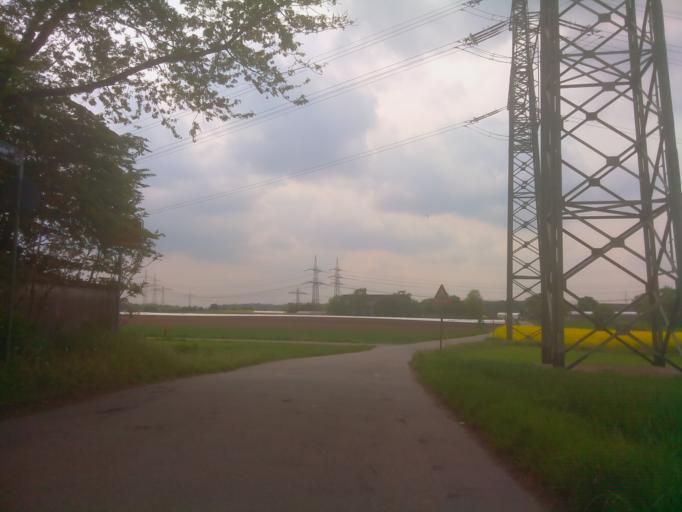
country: DE
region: Baden-Wuerttemberg
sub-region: Karlsruhe Region
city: Edingen-Neckarhausen
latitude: 49.4323
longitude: 8.5795
